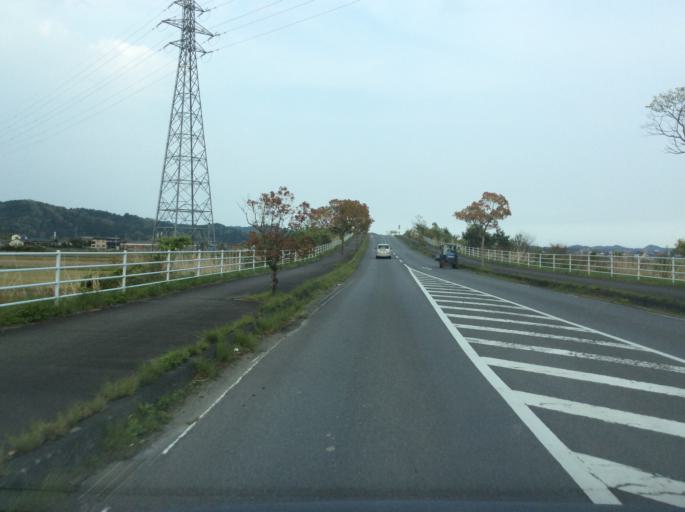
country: JP
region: Fukushima
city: Iwaki
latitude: 37.0701
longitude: 140.8718
